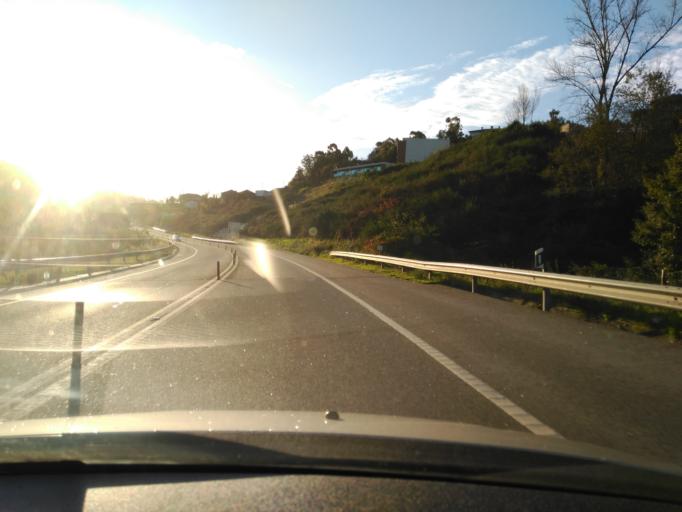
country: PT
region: Braga
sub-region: Guimaraes
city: Guimaraes
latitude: 41.4466
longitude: -8.2564
